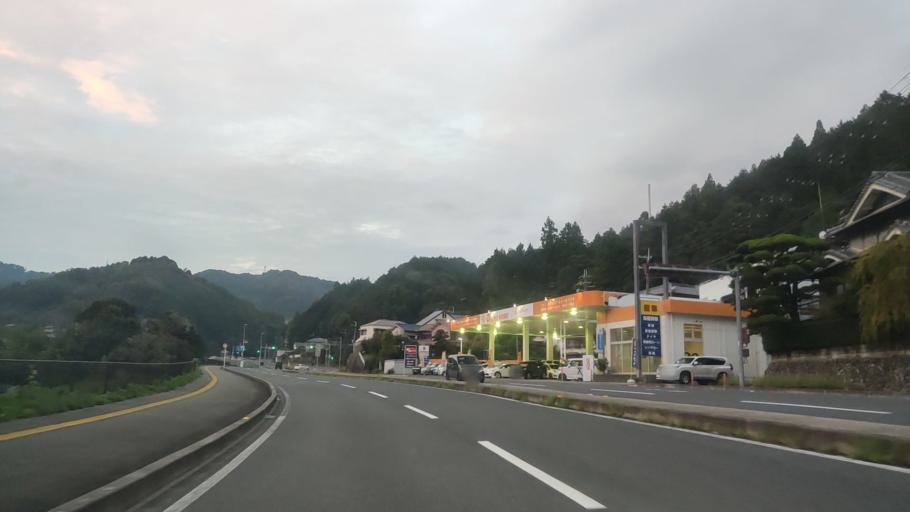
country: JP
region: Wakayama
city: Hashimoto
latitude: 34.3593
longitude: 135.6069
